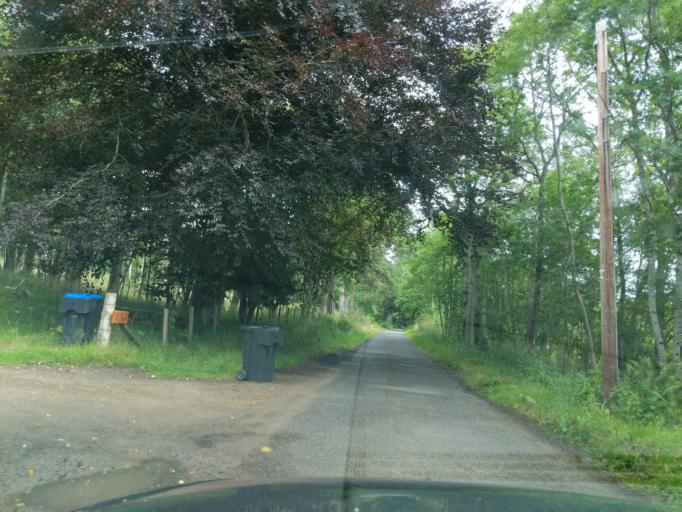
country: GB
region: Scotland
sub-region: Aberdeenshire
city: Aboyne
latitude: 57.0555
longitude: -2.8617
